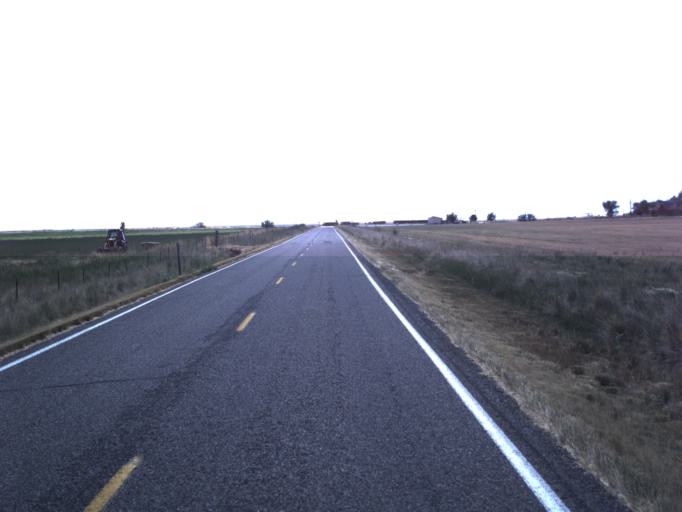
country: US
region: Utah
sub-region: Box Elder County
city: Tremonton
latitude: 41.6327
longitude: -112.3309
